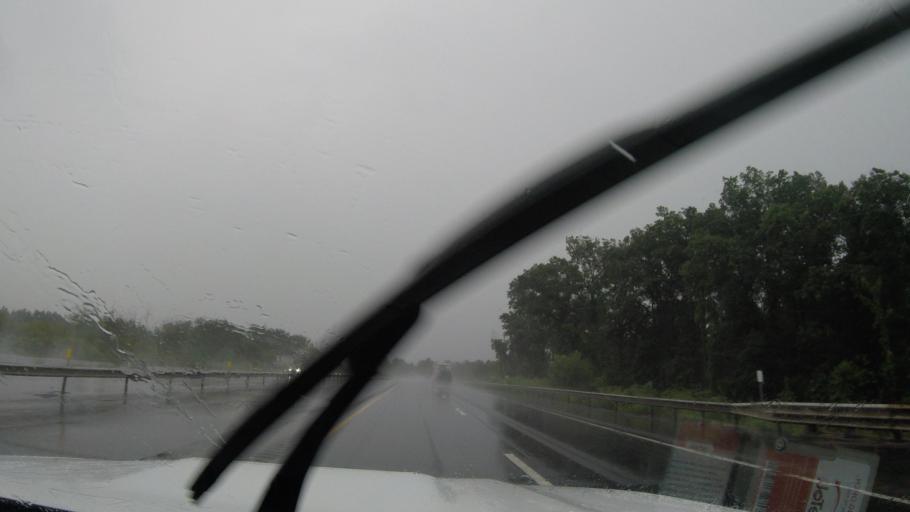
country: US
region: New York
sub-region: Ontario County
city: Phelps
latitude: 42.9548
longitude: -76.9743
